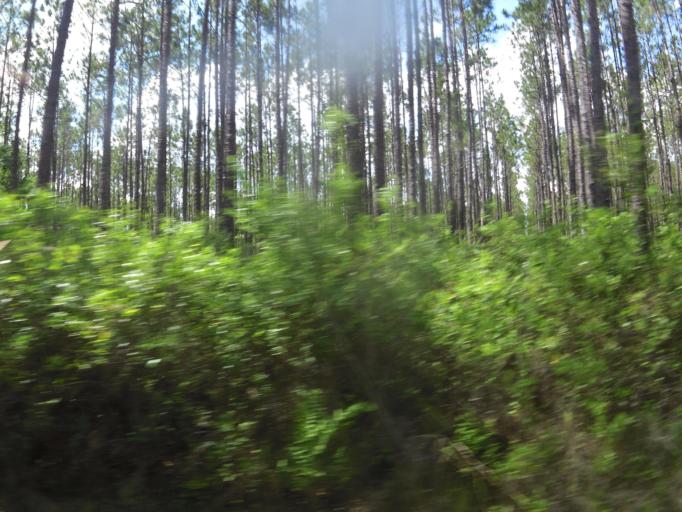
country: US
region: Florida
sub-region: Clay County
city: Asbury Lake
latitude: 29.8635
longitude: -81.8565
